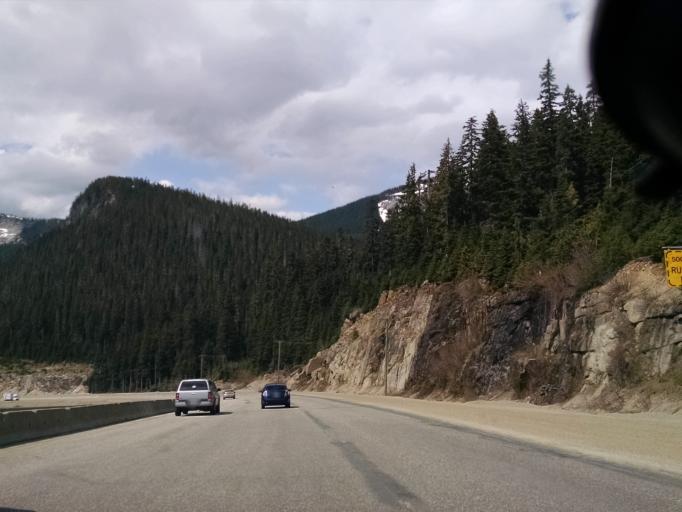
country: CA
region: British Columbia
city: Hope
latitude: 49.5983
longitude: -121.1331
